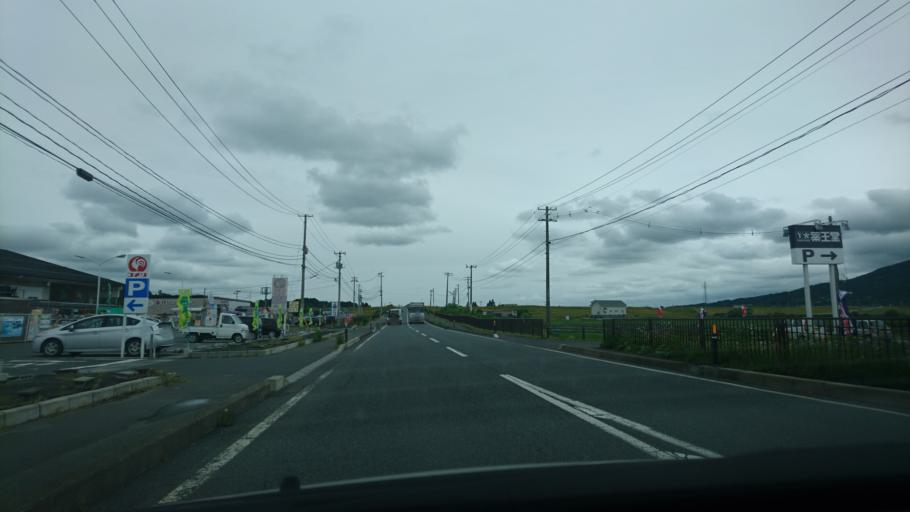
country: JP
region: Iwate
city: Ichinoseki
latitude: 38.9807
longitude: 141.1163
